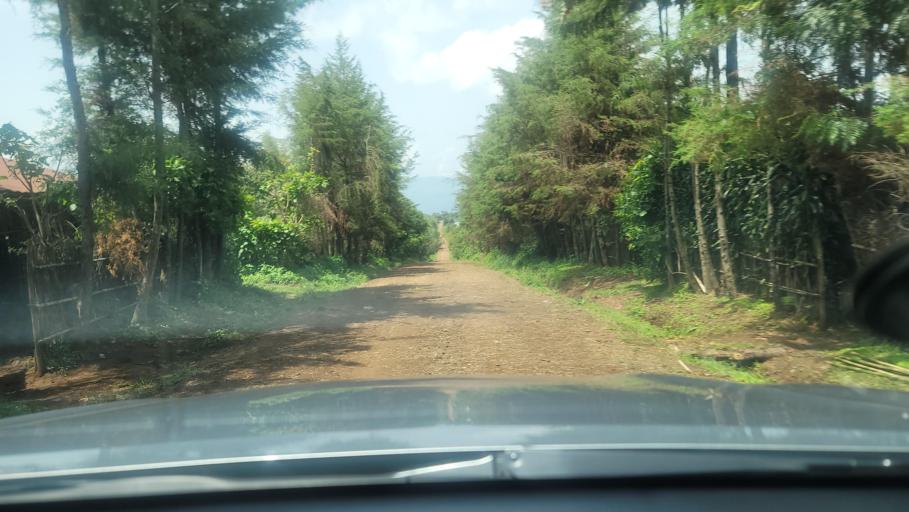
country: ET
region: Oromiya
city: Agaro
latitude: 7.8282
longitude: 36.4074
